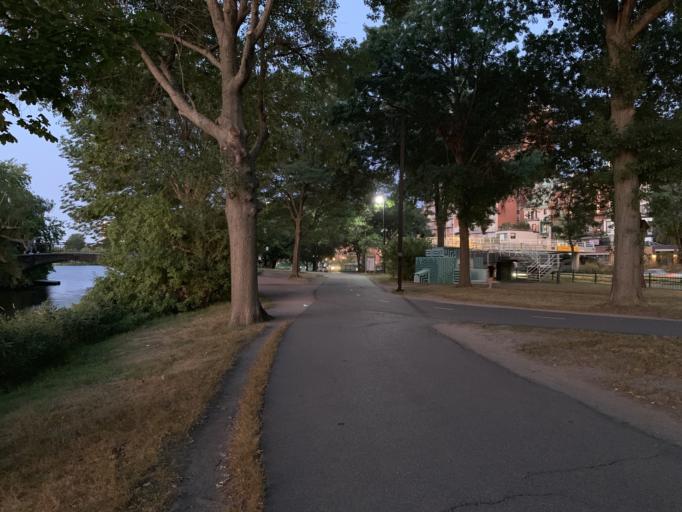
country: US
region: Massachusetts
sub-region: Suffolk County
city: Boston
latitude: 42.3532
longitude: -71.0853
